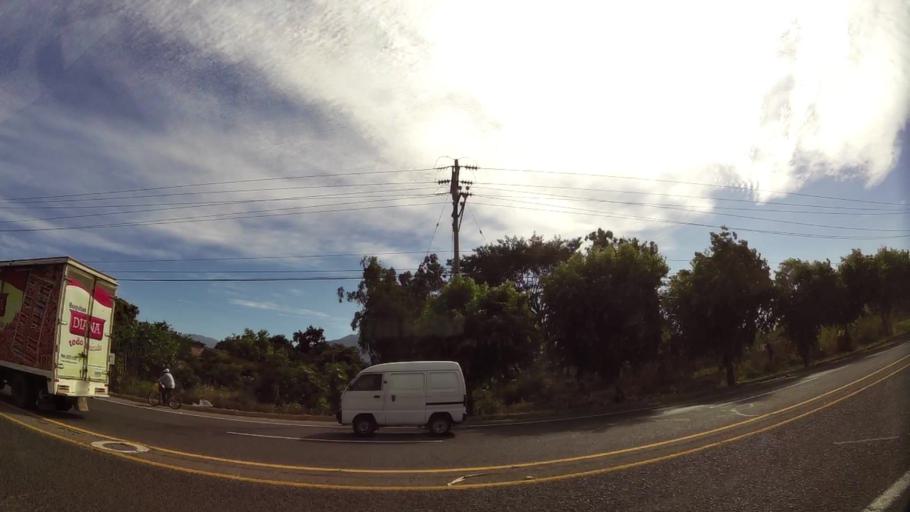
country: SV
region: Santa Ana
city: Chalchuapa
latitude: 13.9879
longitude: -89.6852
